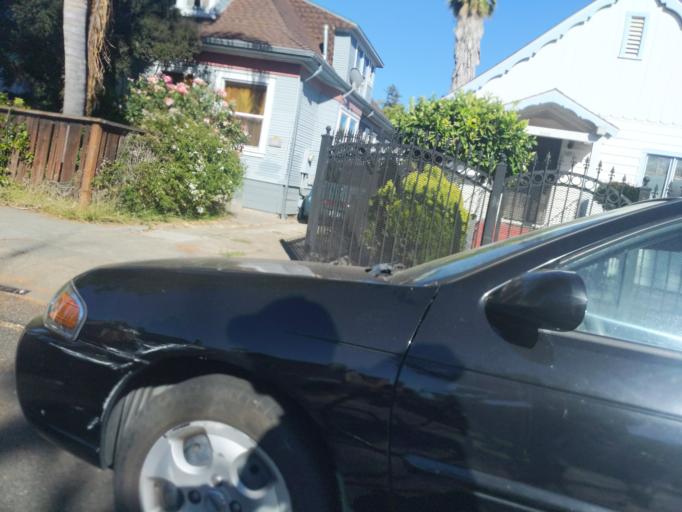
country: US
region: California
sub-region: Alameda County
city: Alameda
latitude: 37.7850
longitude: -122.2199
